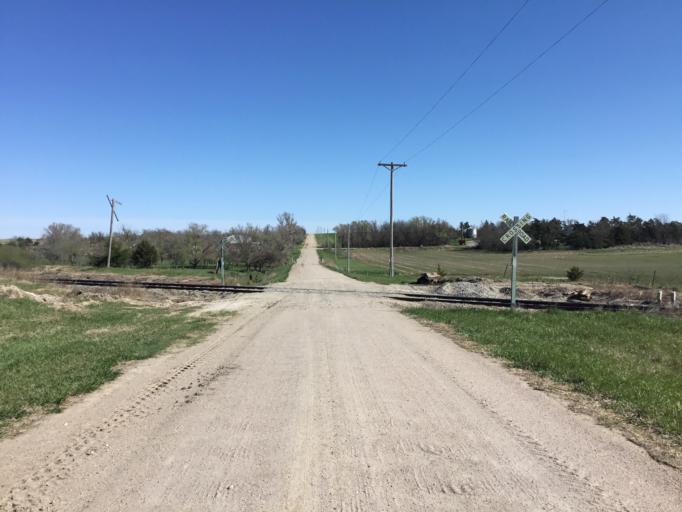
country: US
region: Kansas
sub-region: Norton County
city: Norton
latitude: 39.8486
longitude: -99.6090
